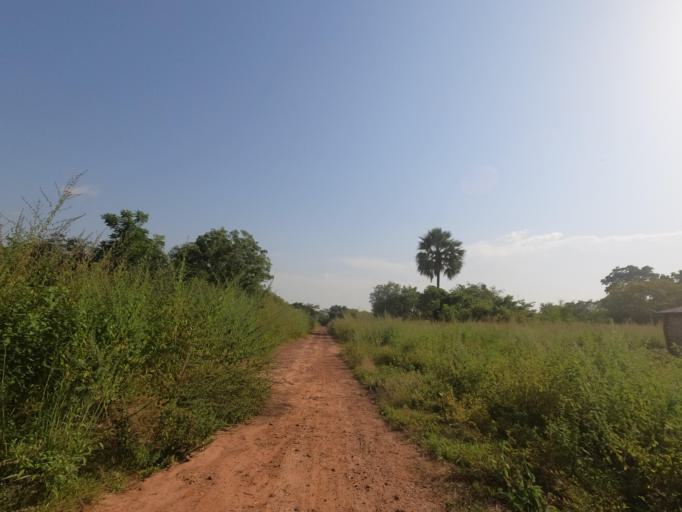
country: SN
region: Sedhiou
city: Sedhiou
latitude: 12.4444
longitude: -15.7390
